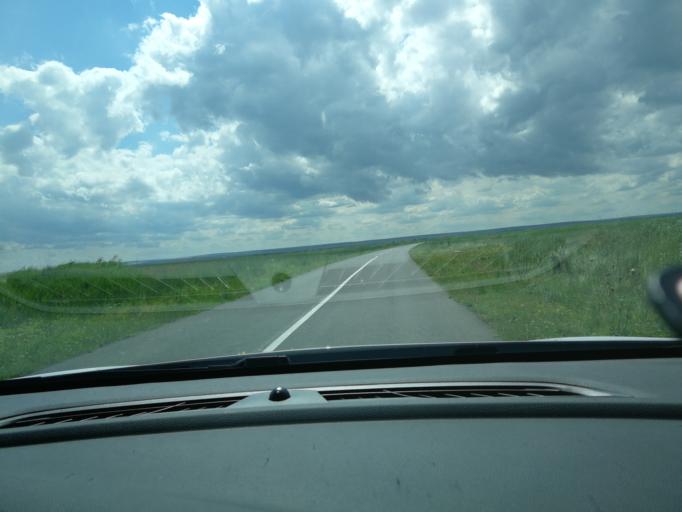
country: RO
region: Constanta
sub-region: Comuna Istria
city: Istria
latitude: 44.5382
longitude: 28.7528
